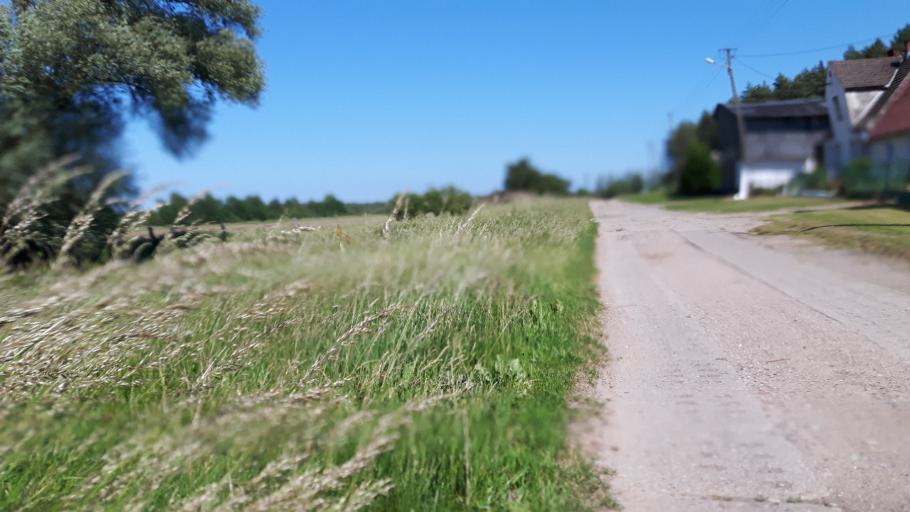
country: PL
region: Pomeranian Voivodeship
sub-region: Powiat slupski
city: Glowczyce
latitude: 54.6421
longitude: 17.3940
